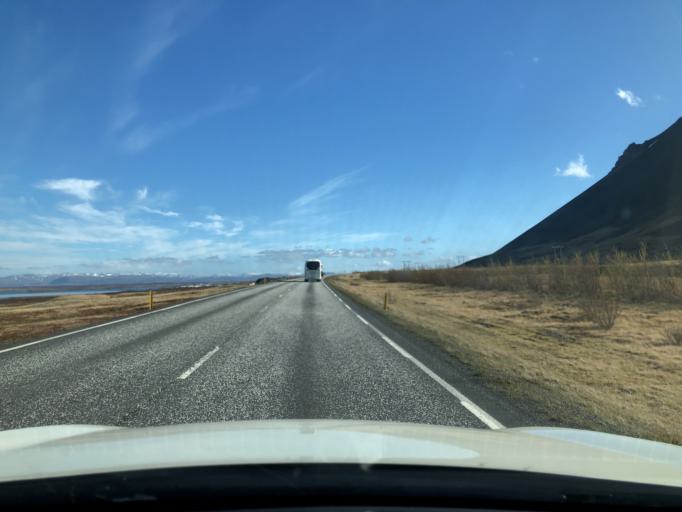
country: IS
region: West
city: Borgarnes
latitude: 64.4903
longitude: -21.9469
